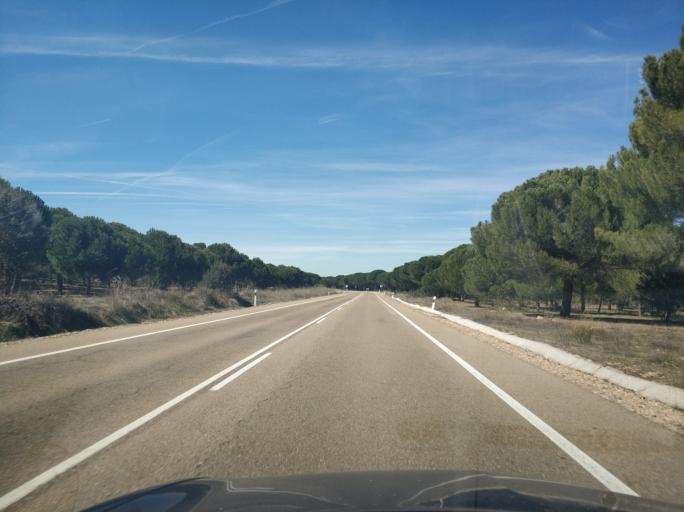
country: ES
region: Castille and Leon
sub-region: Provincia de Valladolid
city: Viana de Cega
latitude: 41.5381
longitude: -4.7674
